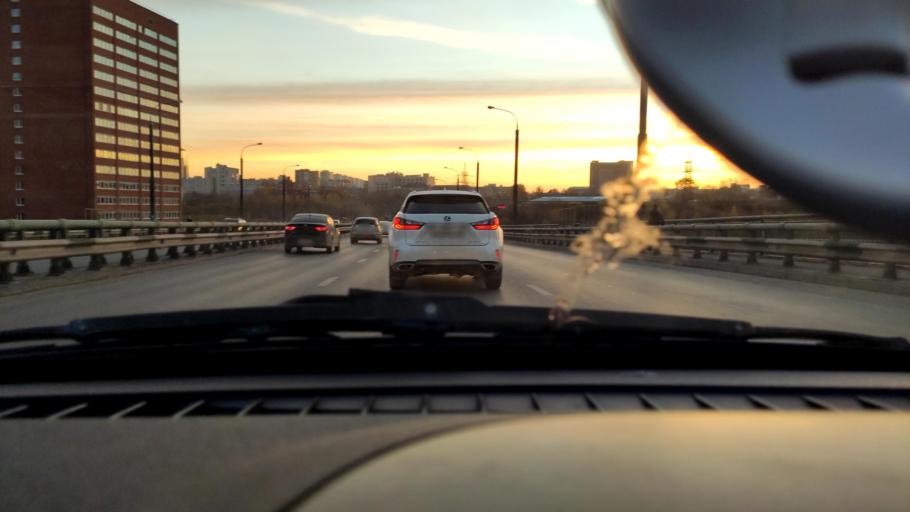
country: RU
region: Perm
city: Perm
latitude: 57.9840
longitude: 56.2294
